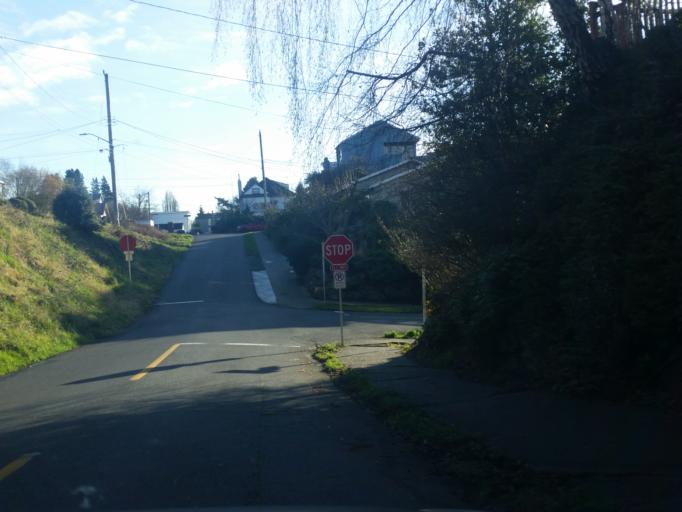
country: US
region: Washington
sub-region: King County
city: Seattle
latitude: 47.6731
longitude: -122.4037
